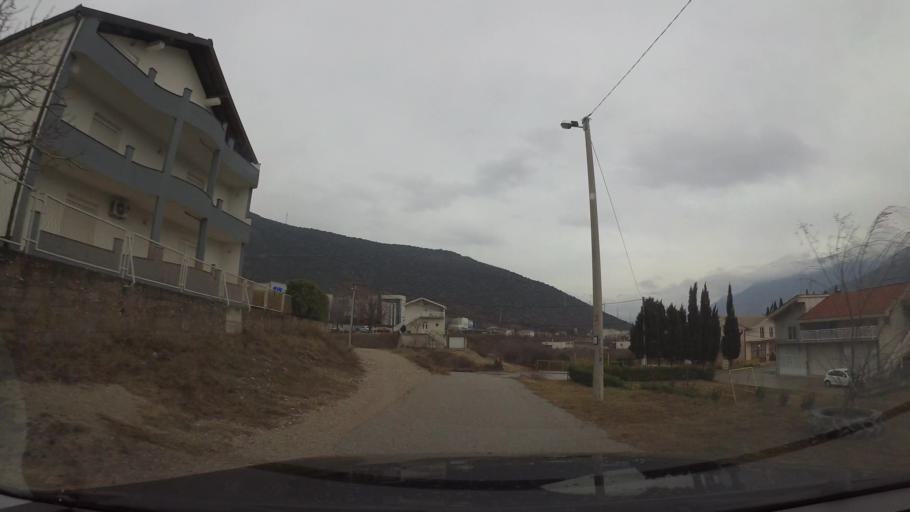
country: BA
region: Federation of Bosnia and Herzegovina
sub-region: Hercegovacko-Bosanski Kanton
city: Mostar
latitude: 43.3659
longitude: 17.8098
